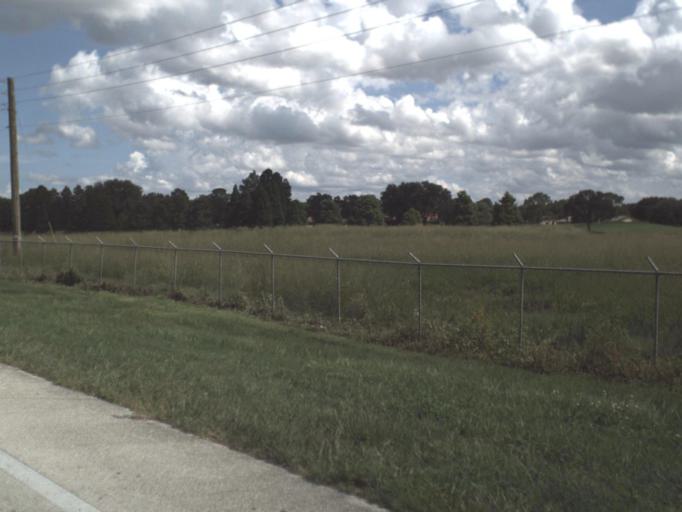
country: US
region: Florida
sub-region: Polk County
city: Dundee
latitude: 28.0188
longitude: -81.6512
